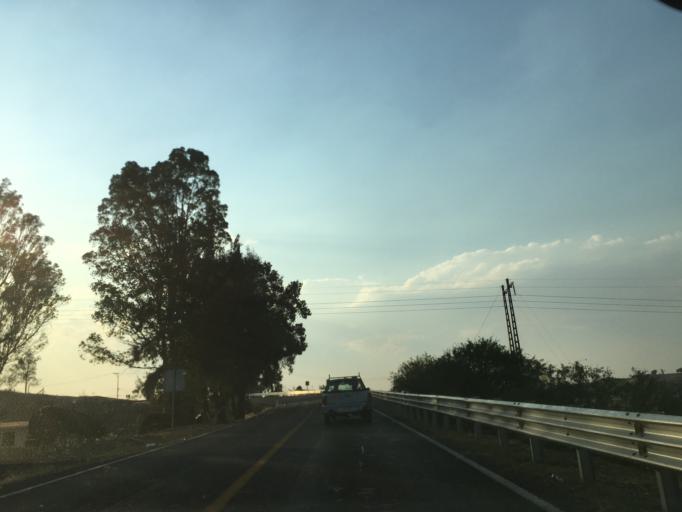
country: MX
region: Michoacan
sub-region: Morelia
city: La Aldea
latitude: 19.7370
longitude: -101.1072
